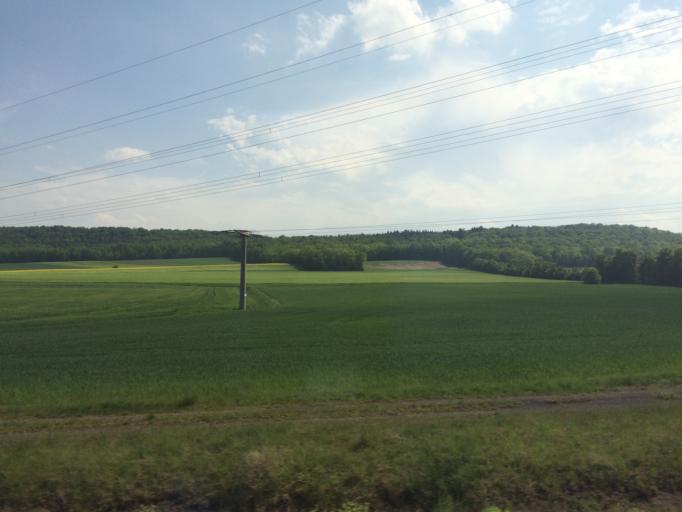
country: DE
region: Bavaria
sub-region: Regierungsbezirk Mittelfranken
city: Scheinfeld
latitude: 49.6416
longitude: 10.4589
